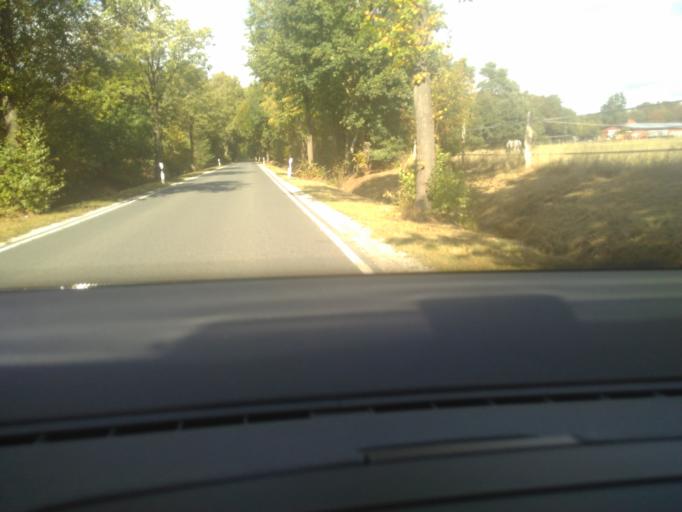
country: DE
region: North Rhine-Westphalia
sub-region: Regierungsbezirk Detmold
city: Verl
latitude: 51.9395
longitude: 8.5148
